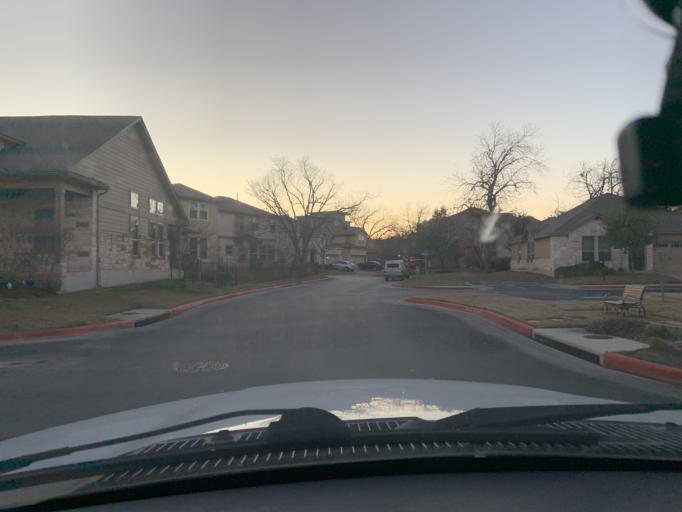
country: US
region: Texas
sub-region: Williamson County
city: Anderson Mill
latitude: 30.4631
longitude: -97.8016
